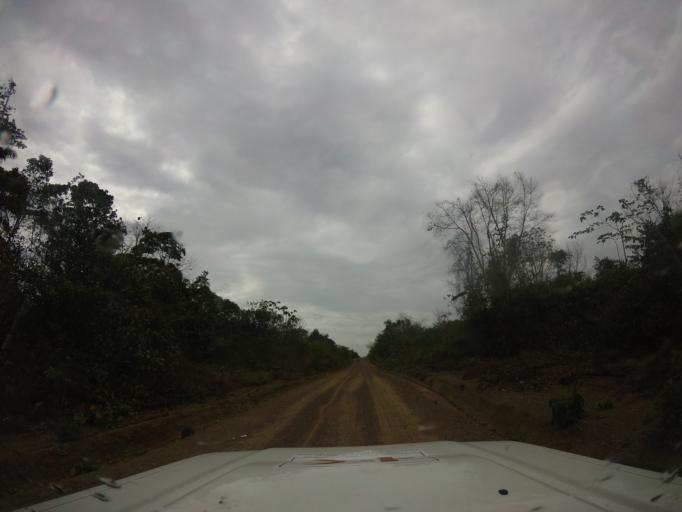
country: SL
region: Southern Province
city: Zimmi
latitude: 7.2262
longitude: -11.1917
